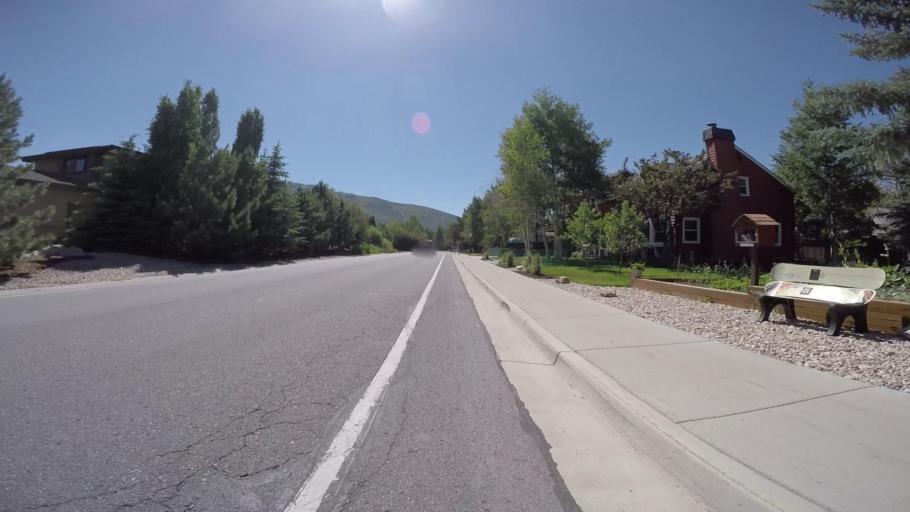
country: US
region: Utah
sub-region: Summit County
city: Park City
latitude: 40.6719
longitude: -111.5067
